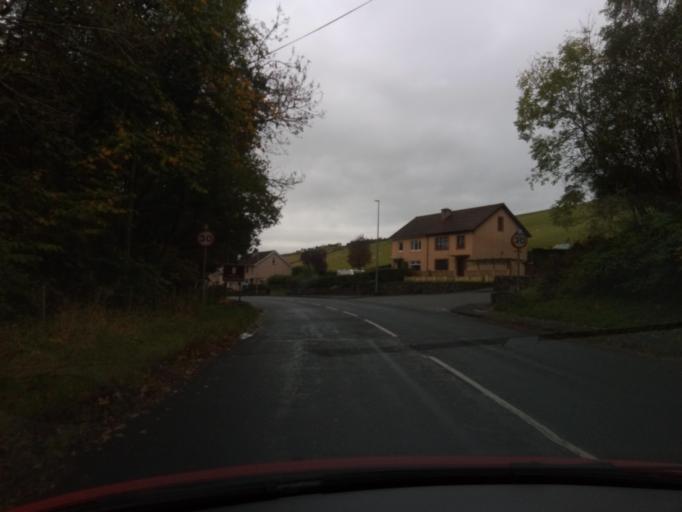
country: GB
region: Scotland
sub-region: The Scottish Borders
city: Galashiels
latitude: 55.6284
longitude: -2.8388
